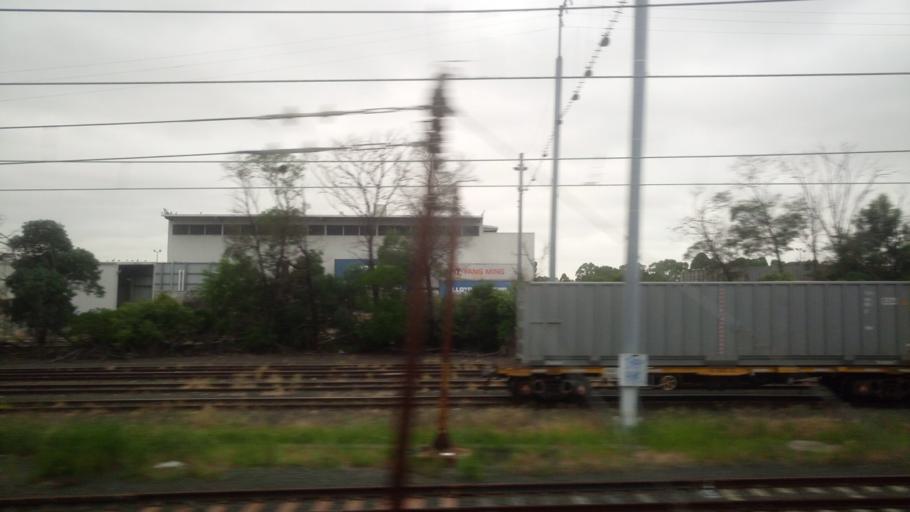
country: AU
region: New South Wales
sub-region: Parramatta
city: Granville
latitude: -33.8387
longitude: 151.0214
